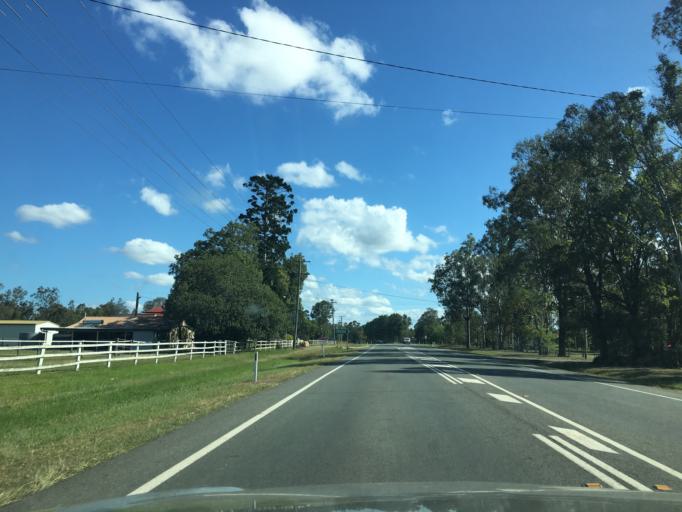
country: AU
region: Queensland
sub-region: Logan
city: Waterford West
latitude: -27.7129
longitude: 153.1303
